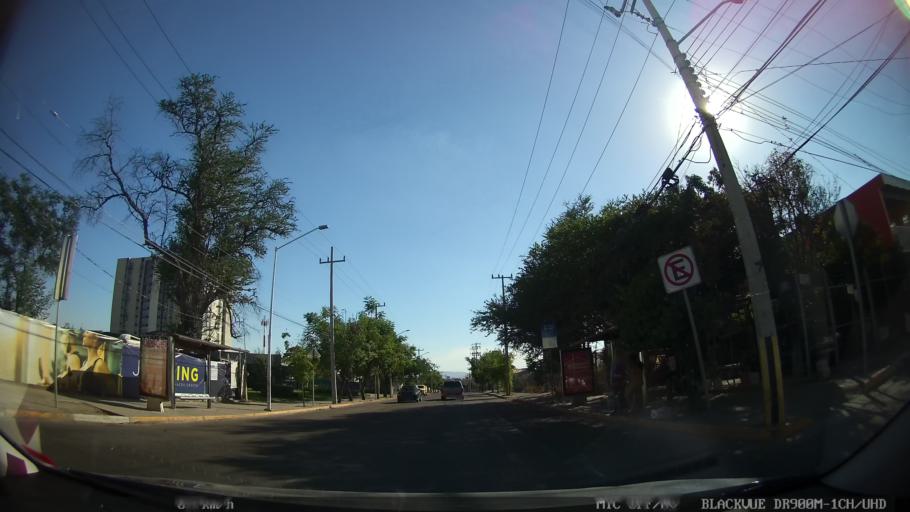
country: MX
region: Jalisco
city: Tlaquepaque
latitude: 20.7135
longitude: -103.3027
